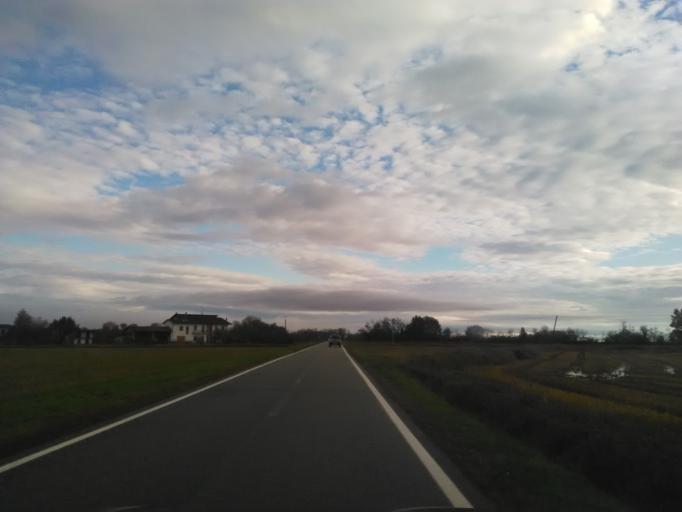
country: IT
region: Piedmont
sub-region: Provincia di Vercelli
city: Rovasenda
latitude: 45.5405
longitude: 8.3266
